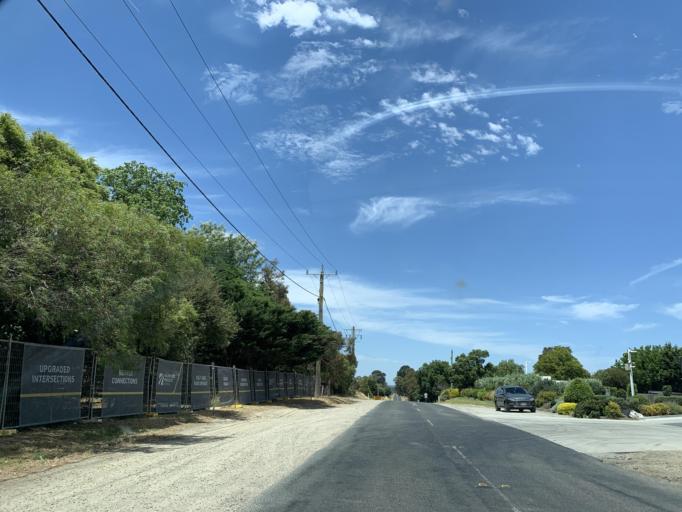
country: AU
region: Victoria
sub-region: Mornington Peninsula
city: Langwarrin South
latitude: -38.1994
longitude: 145.1821
